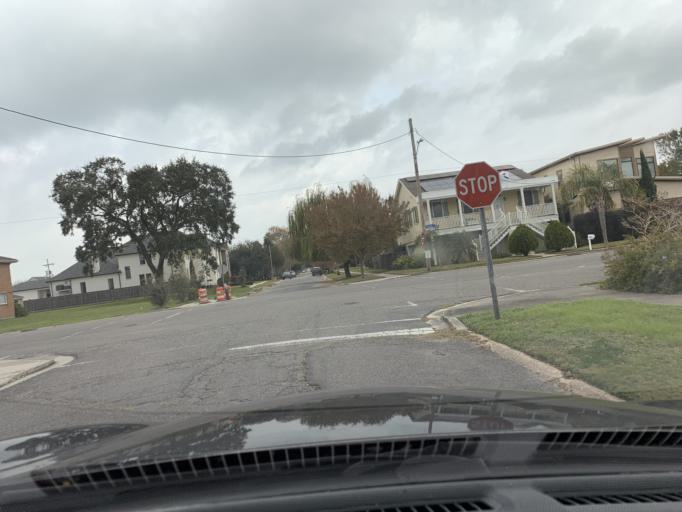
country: US
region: Louisiana
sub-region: Jefferson Parish
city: Metairie
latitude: 30.0114
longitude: -90.1007
